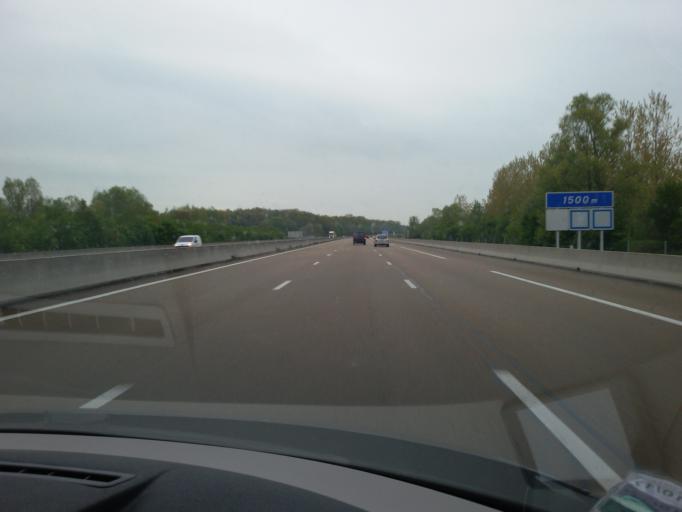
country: FR
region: Bourgogne
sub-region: Departement de la Cote-d'Or
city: Saint-Julien
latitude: 47.4085
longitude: 5.1803
